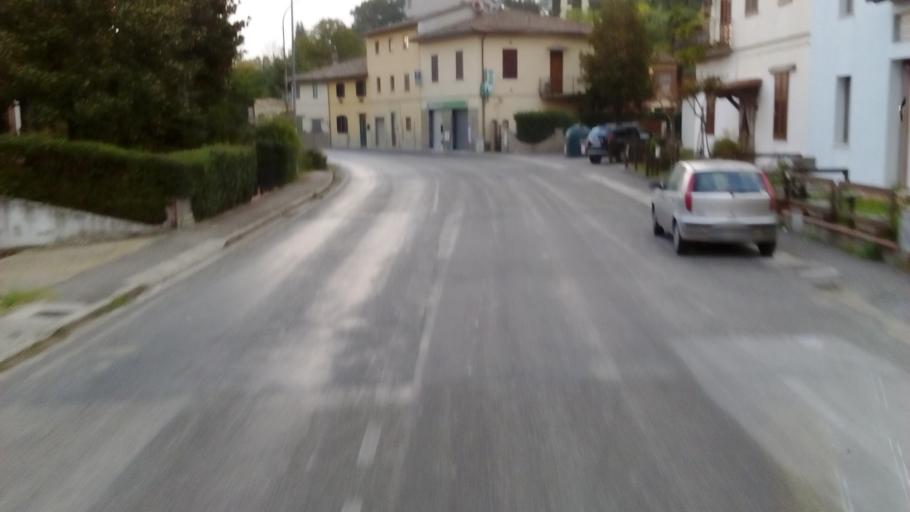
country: IT
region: Tuscany
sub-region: Province of Florence
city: Castelfiorentino
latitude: 43.6326
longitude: 10.9605
